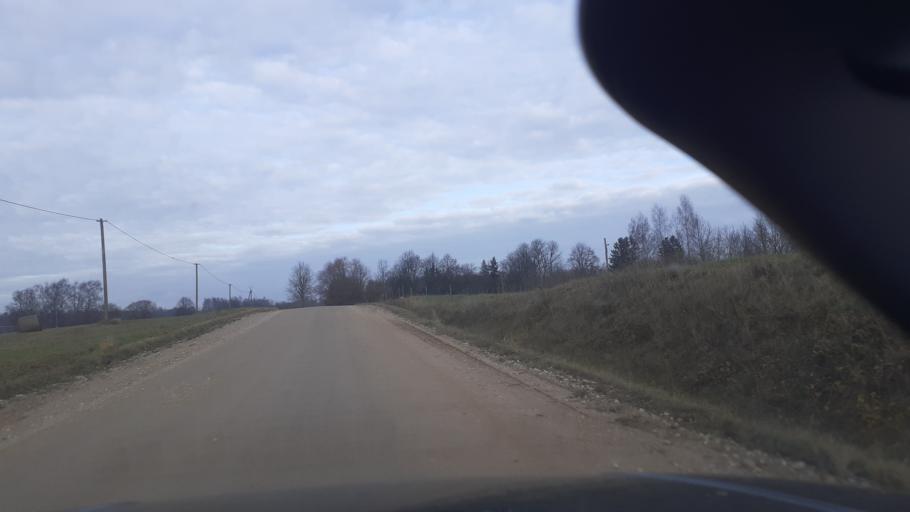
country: LV
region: Alsunga
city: Alsunga
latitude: 56.9066
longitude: 21.6553
